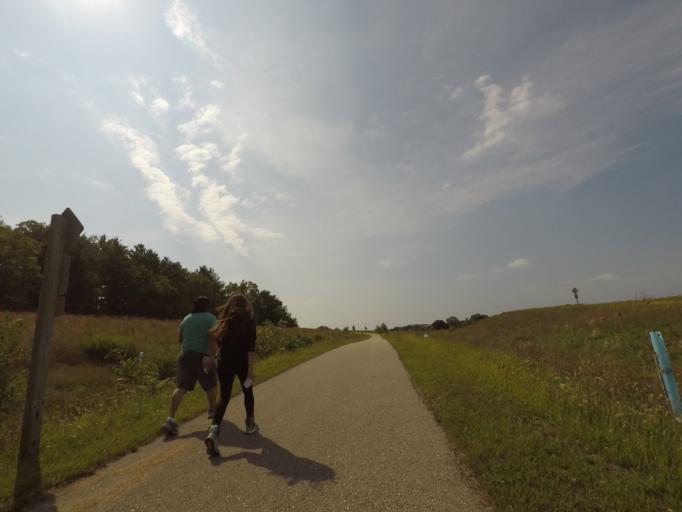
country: US
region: Wisconsin
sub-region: Jefferson County
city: Jefferson
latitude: 42.9871
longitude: -88.8293
